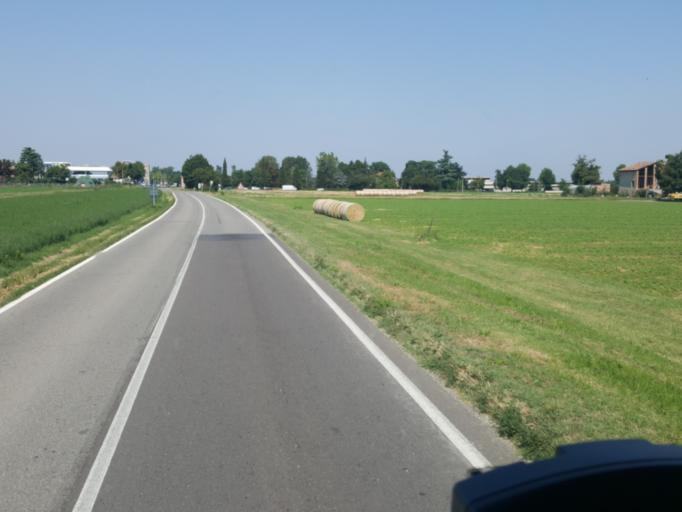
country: IT
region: Emilia-Romagna
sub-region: Provincia di Modena
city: San Vito
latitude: 44.5378
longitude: 10.9734
